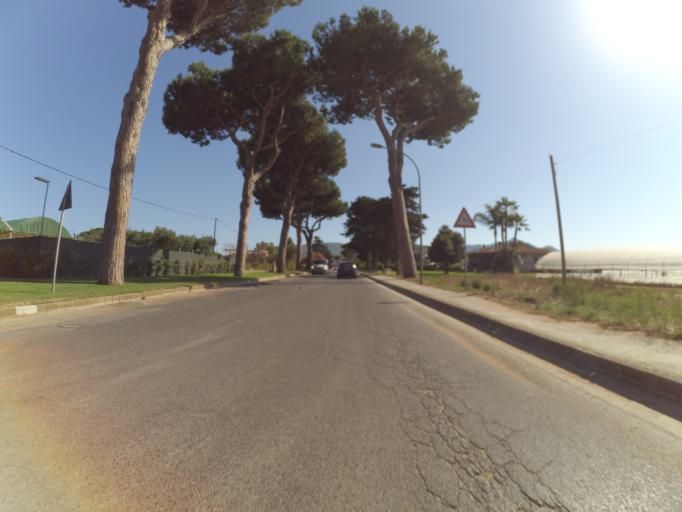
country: IT
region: Latium
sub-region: Provincia di Latina
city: San Felice Circeo
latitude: 41.2635
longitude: 13.0937
